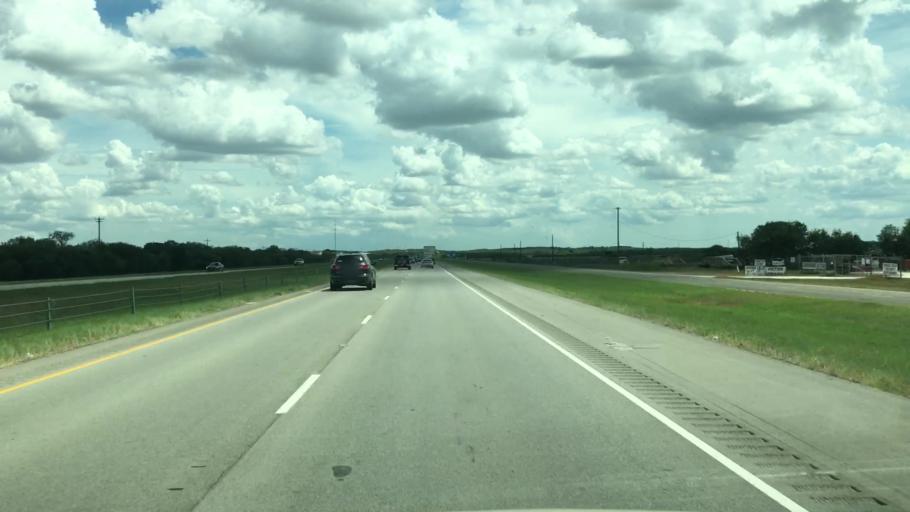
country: US
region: Texas
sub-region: Live Oak County
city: George West
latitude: 28.2722
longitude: -97.9456
